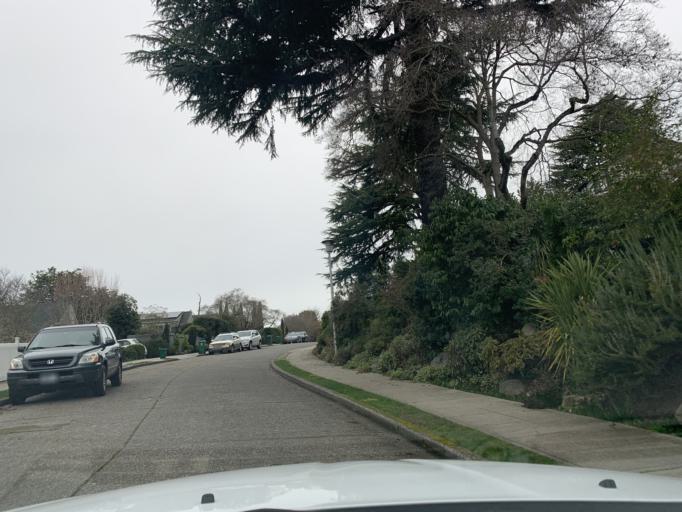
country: US
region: Washington
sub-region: King County
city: Medina
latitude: 47.6542
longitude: -122.2780
